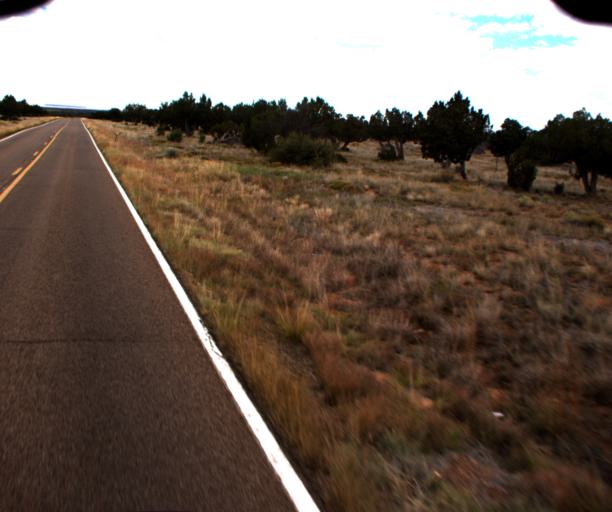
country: US
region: Arizona
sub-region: Navajo County
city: Heber-Overgaard
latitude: 34.4978
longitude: -110.4542
